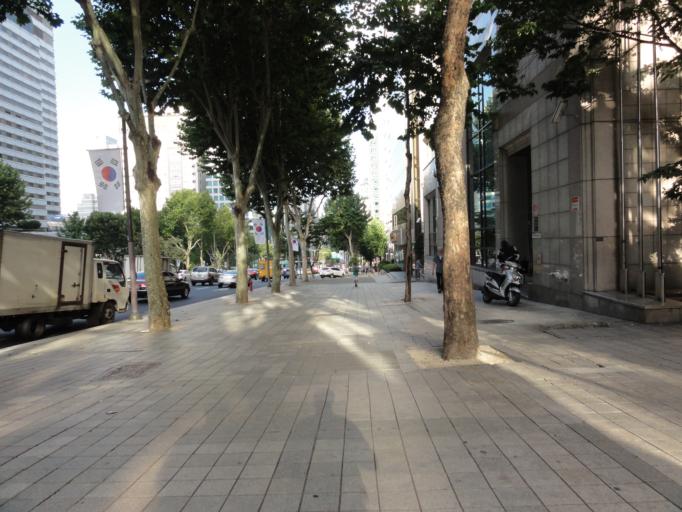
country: KR
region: Seoul
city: Seoul
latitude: 37.5022
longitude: 127.0394
